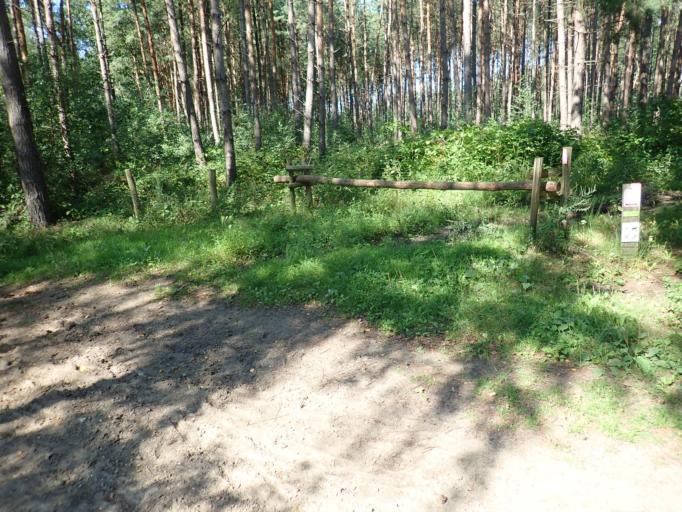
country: BE
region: Flanders
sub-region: Provincie Vlaams-Brabant
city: Scherpenheuvel-Zichem
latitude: 51.0312
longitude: 4.9584
